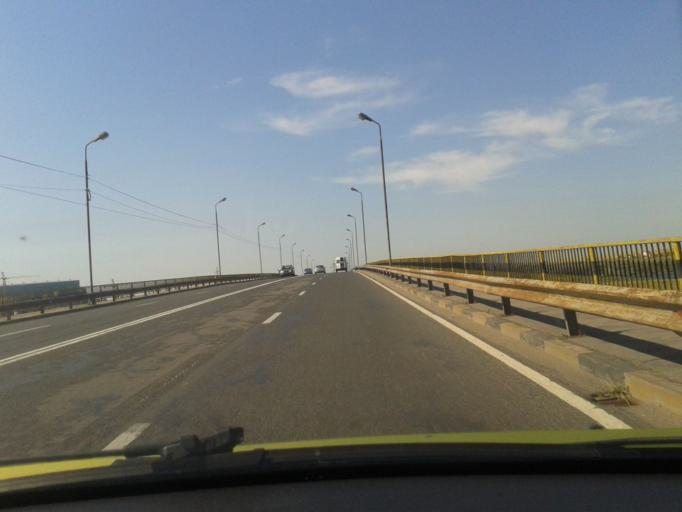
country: RO
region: Constanta
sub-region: Municipiul Mangalia
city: Mangalia
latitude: 43.8053
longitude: 28.5606
